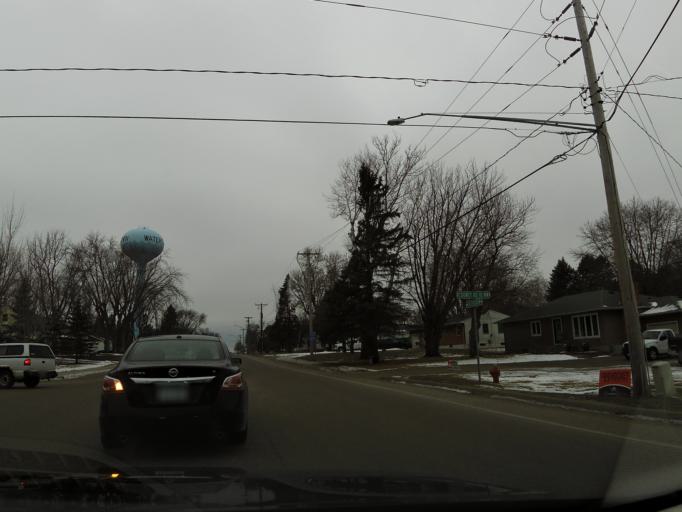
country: US
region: Minnesota
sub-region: Carver County
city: Watertown
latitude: 44.9661
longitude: -93.8523
